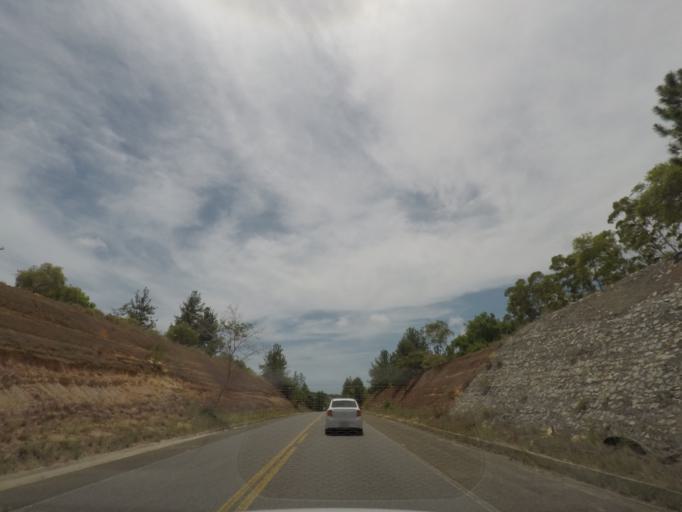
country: BR
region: Bahia
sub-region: Conde
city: Conde
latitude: -12.0081
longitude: -37.6863
